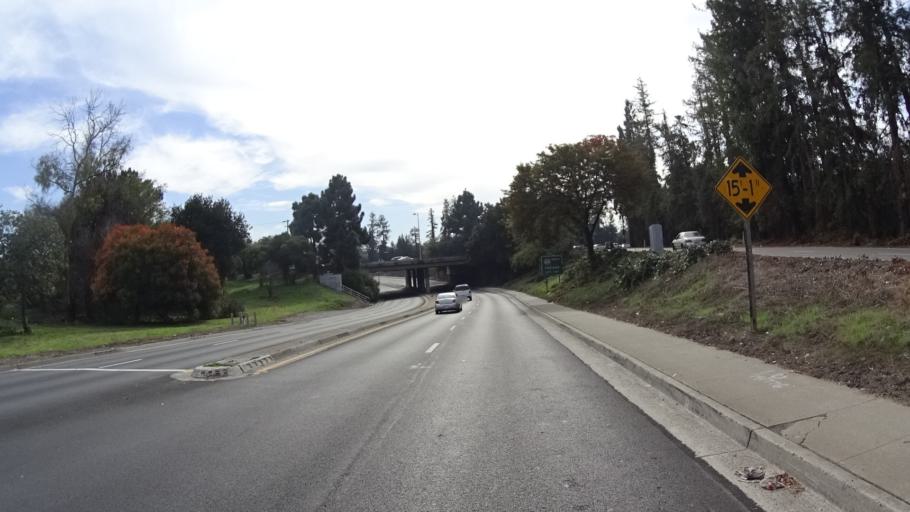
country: US
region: California
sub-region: Santa Clara County
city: Burbank
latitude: 37.3356
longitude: -121.9368
